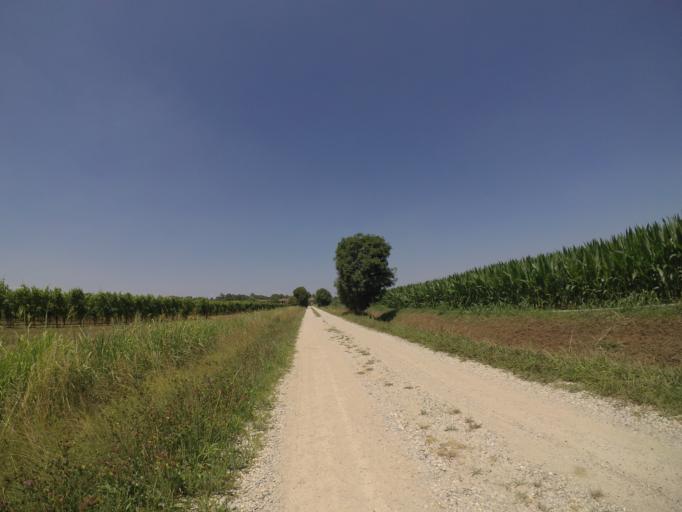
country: IT
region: Friuli Venezia Giulia
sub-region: Provincia di Udine
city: Bertiolo
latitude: 45.9447
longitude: 13.0156
